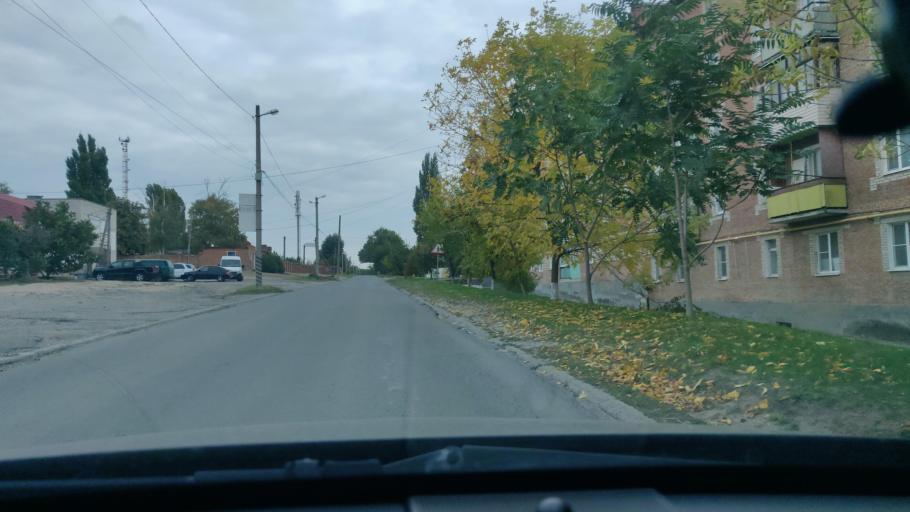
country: RU
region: Rostov
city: Ust'-Donetskiy
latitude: 47.6473
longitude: 40.8624
